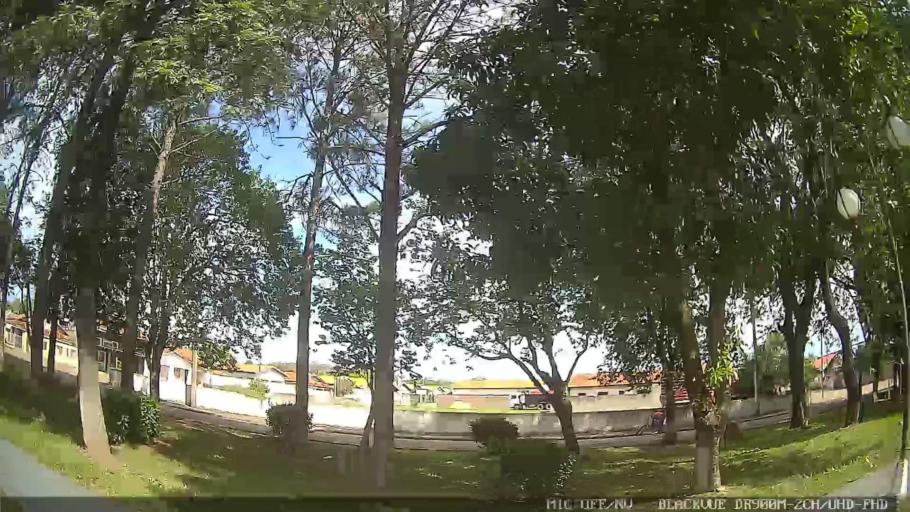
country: BR
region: Sao Paulo
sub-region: Conchas
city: Conchas
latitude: -23.0680
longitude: -47.9757
